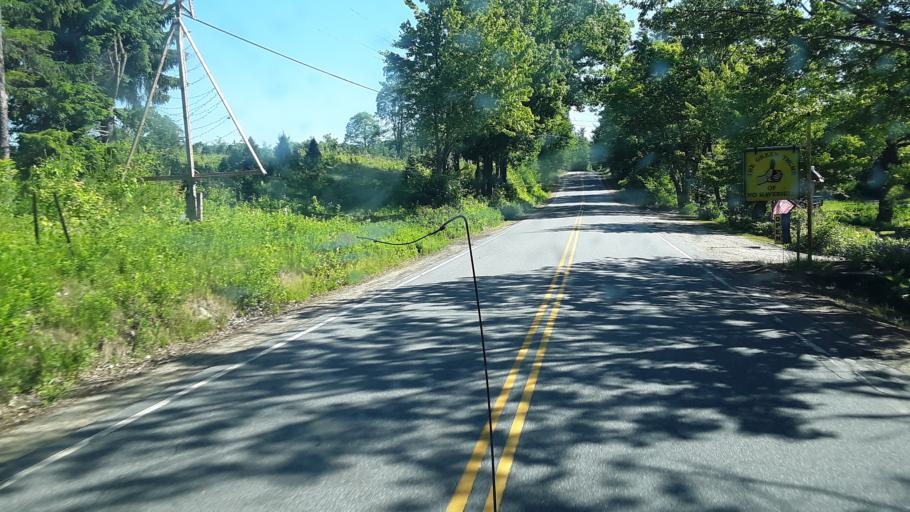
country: US
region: New Hampshire
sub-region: Grafton County
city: North Haverhill
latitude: 44.0930
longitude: -71.9454
